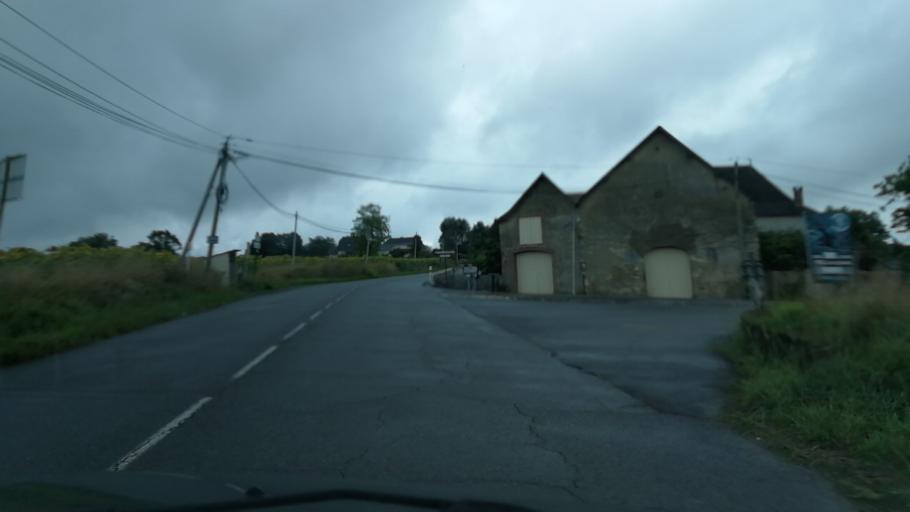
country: FR
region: Aquitaine
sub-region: Departement des Pyrenees-Atlantiques
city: Lucq-de-Bearn
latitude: 43.2974
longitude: -0.6640
